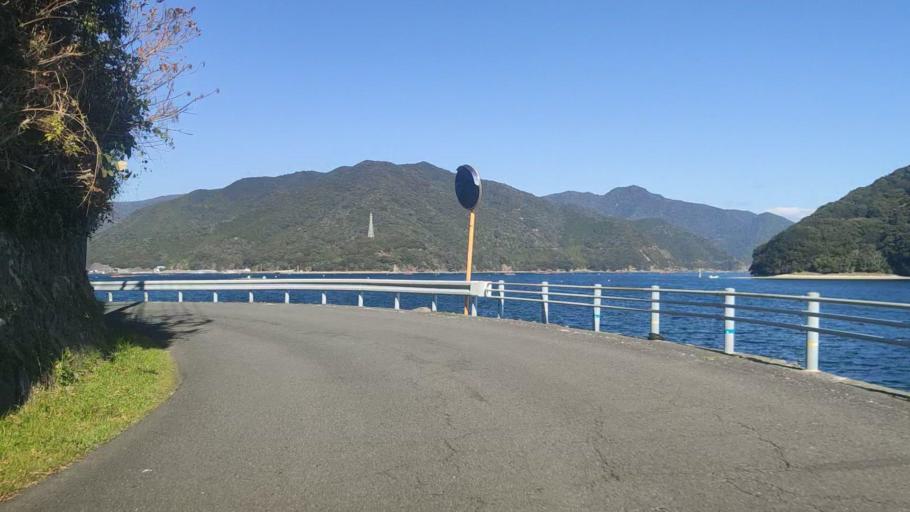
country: JP
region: Oita
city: Saiki
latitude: 32.8333
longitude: 131.9599
